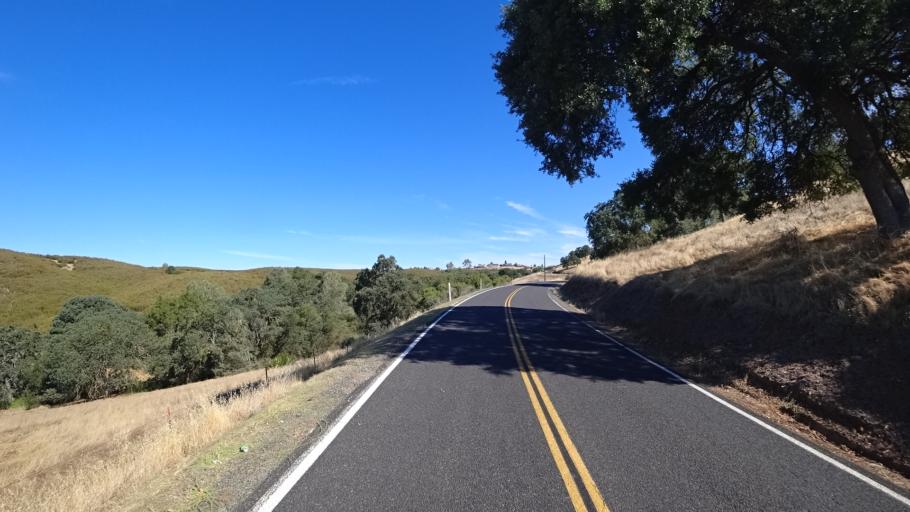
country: US
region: California
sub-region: Calaveras County
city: Valley Springs
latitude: 38.1547
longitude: -120.8167
